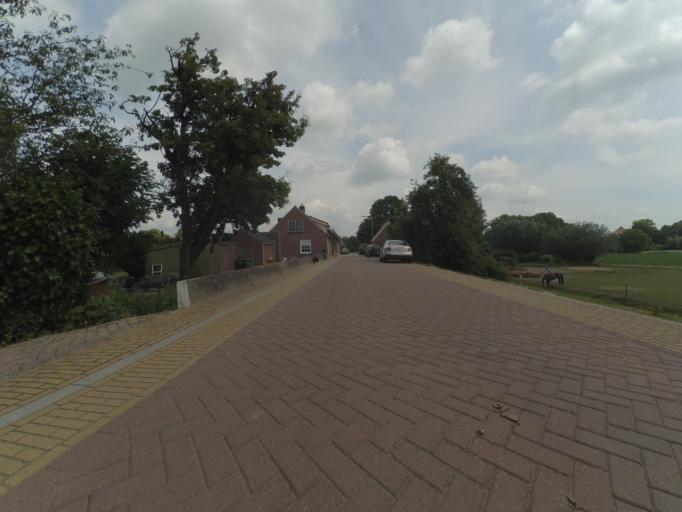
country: NL
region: North Brabant
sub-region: Gemeente Woudrichem
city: Almkerk
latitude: 51.7658
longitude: 4.9198
